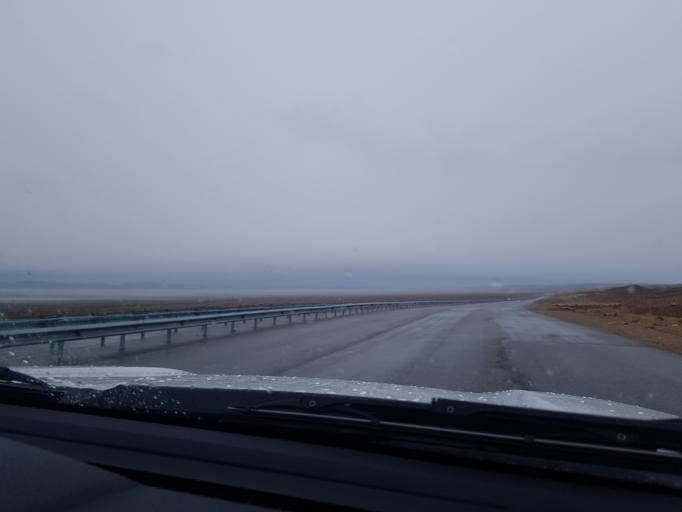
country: TM
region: Balkan
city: Turkmenbasy
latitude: 40.0393
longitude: 53.4612
